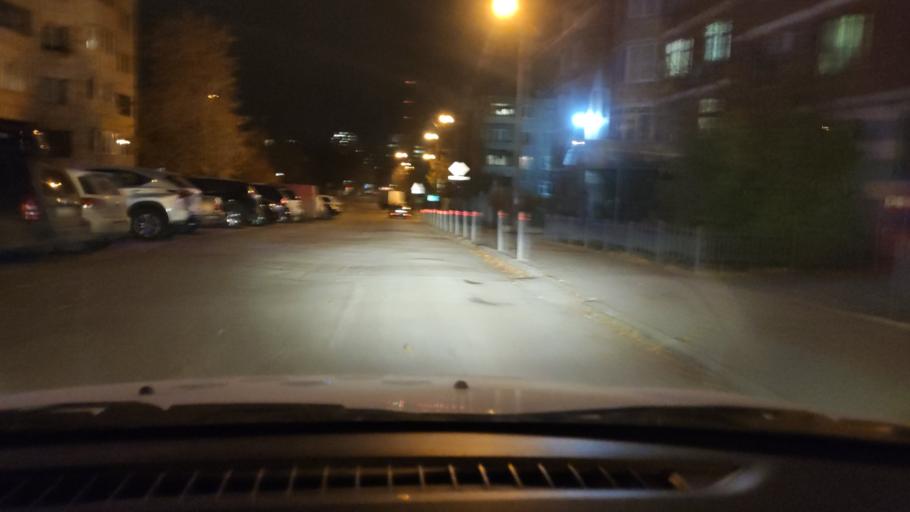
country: RU
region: Perm
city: Perm
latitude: 58.0068
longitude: 56.2701
